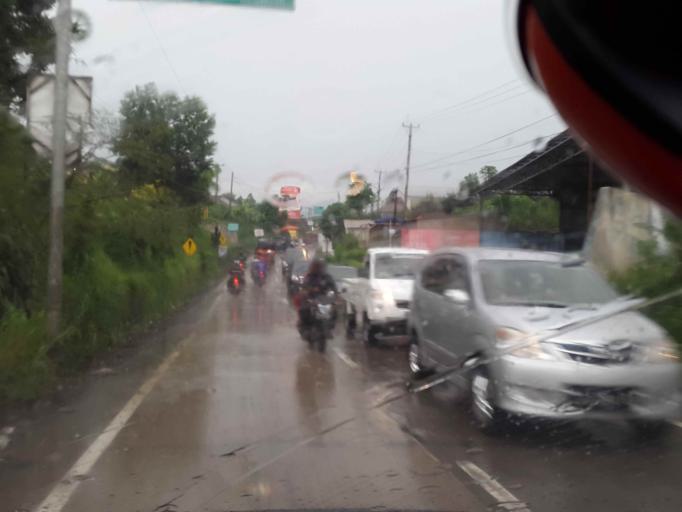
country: ID
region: West Java
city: Cimahi
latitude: -6.9337
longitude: 107.5055
